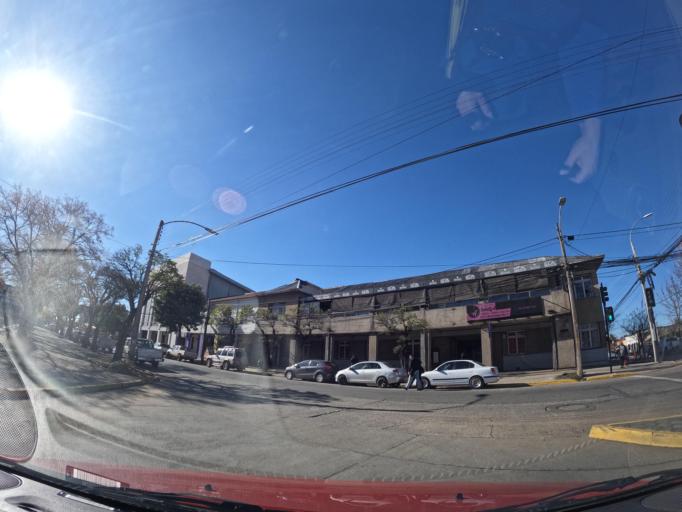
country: CL
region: Maule
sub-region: Provincia de Cauquenes
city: Cauquenes
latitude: -35.9675
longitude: -72.3148
